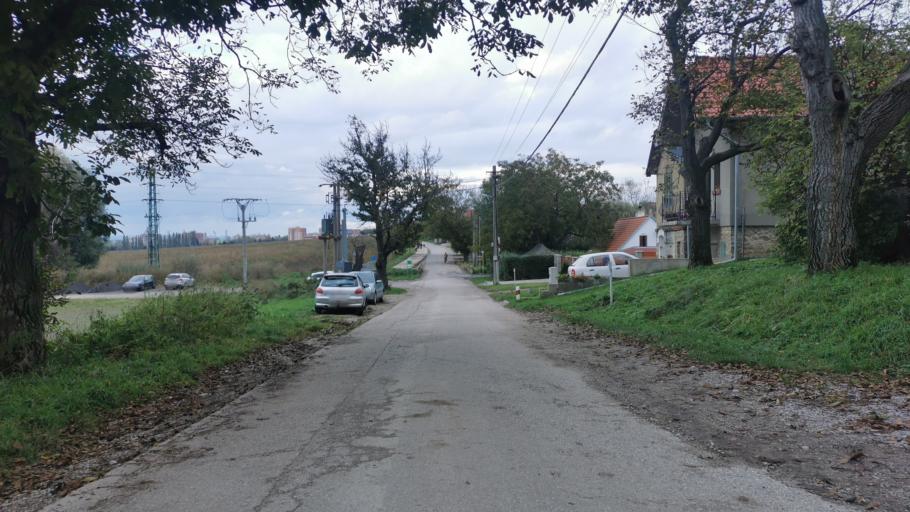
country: SK
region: Trnavsky
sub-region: Okres Skalica
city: Skalica
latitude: 48.8259
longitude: 17.2232
